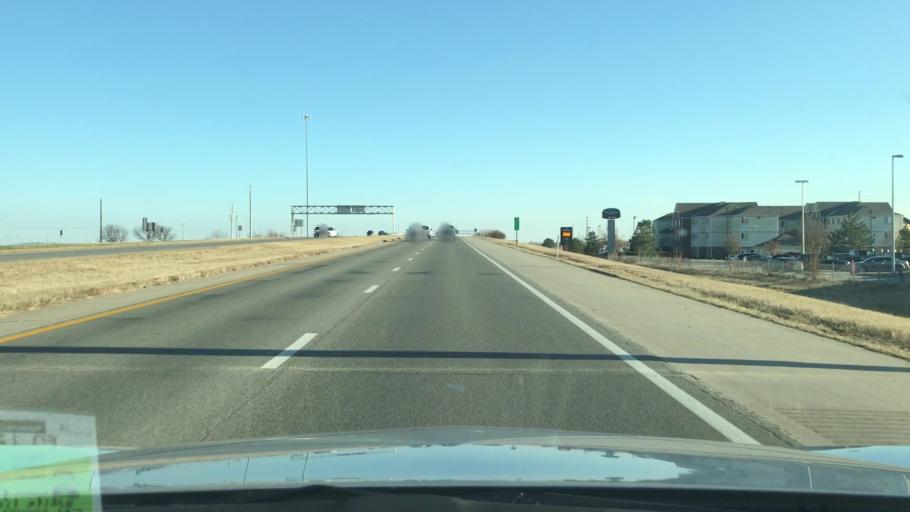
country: US
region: Kansas
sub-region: Sedgwick County
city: Bellaire
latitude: 37.7399
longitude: -97.2292
